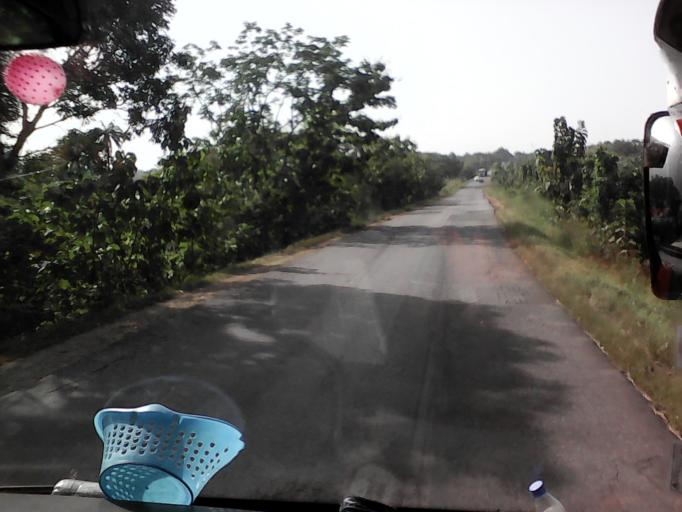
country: TG
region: Centrale
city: Sokode
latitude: 9.0503
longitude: 1.1348
